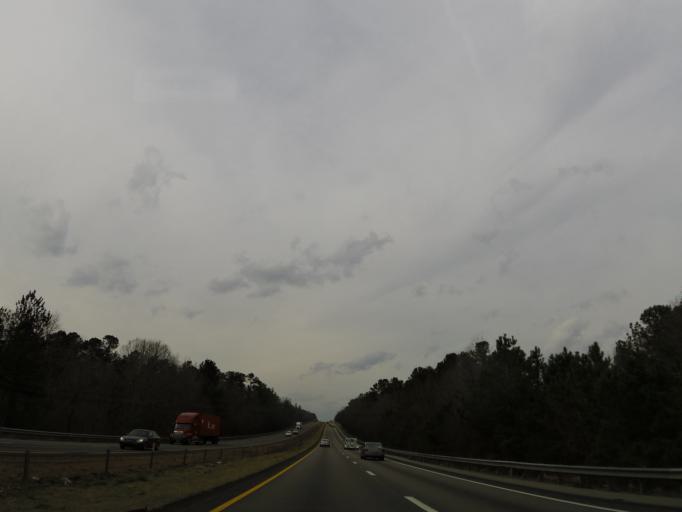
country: US
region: South Carolina
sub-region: Calhoun County
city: Oak Grove
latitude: 33.7213
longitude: -80.9264
